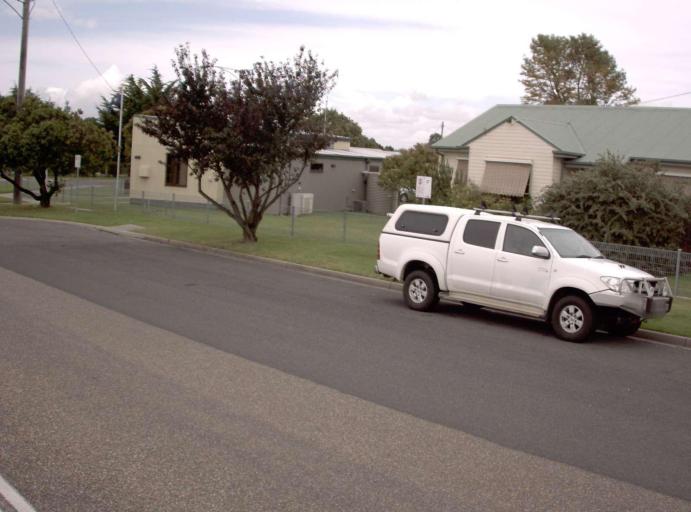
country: AU
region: Victoria
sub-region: Wellington
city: Sale
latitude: -37.9632
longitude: 147.0806
